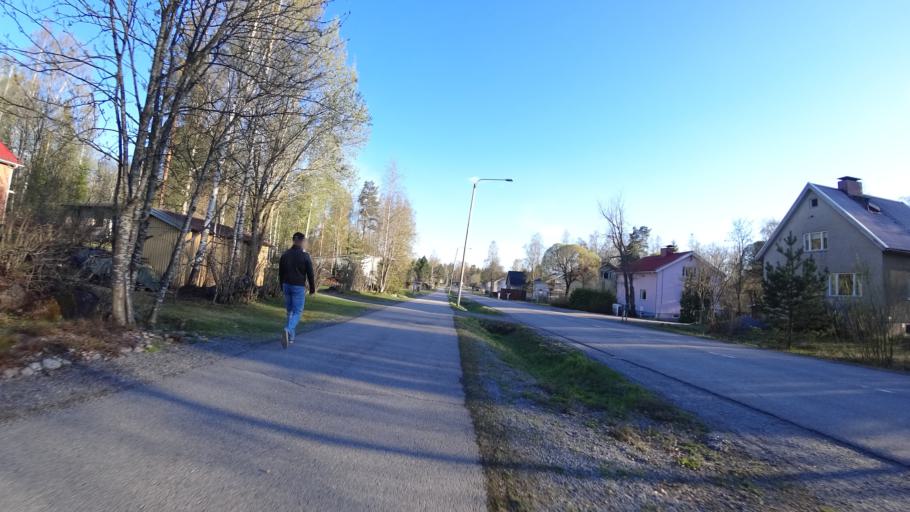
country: FI
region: Pirkanmaa
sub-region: Tampere
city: Yloejaervi
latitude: 61.5086
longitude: 23.5939
